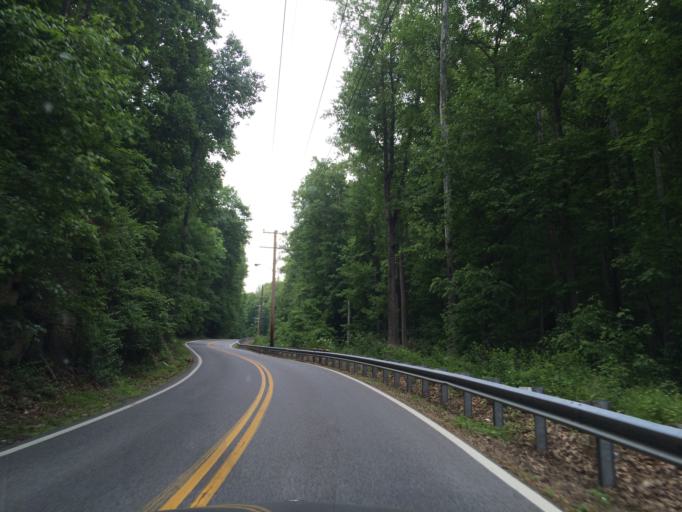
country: US
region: Maryland
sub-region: Baltimore County
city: Randallstown
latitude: 39.3701
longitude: -76.8761
